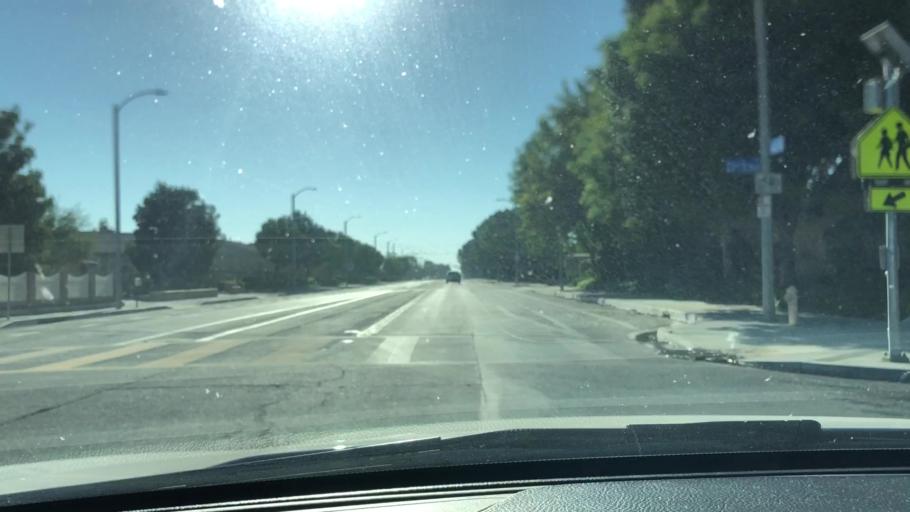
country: US
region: California
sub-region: Los Angeles County
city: Lancaster
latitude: 34.6676
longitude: -118.1701
